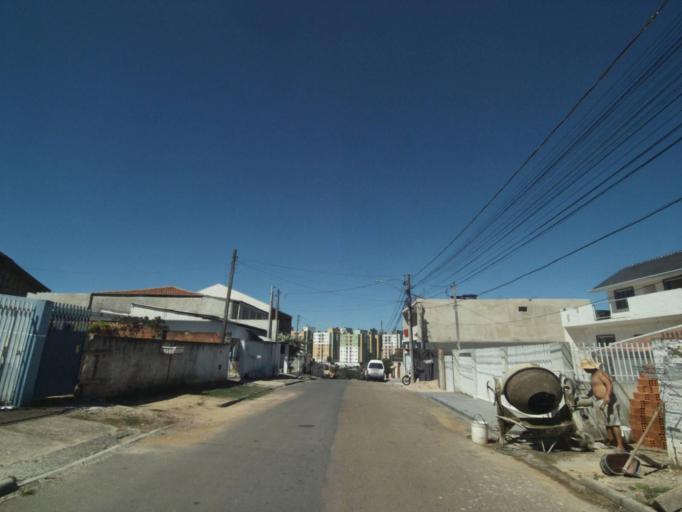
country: BR
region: Parana
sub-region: Curitiba
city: Curitiba
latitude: -25.4629
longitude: -49.3413
